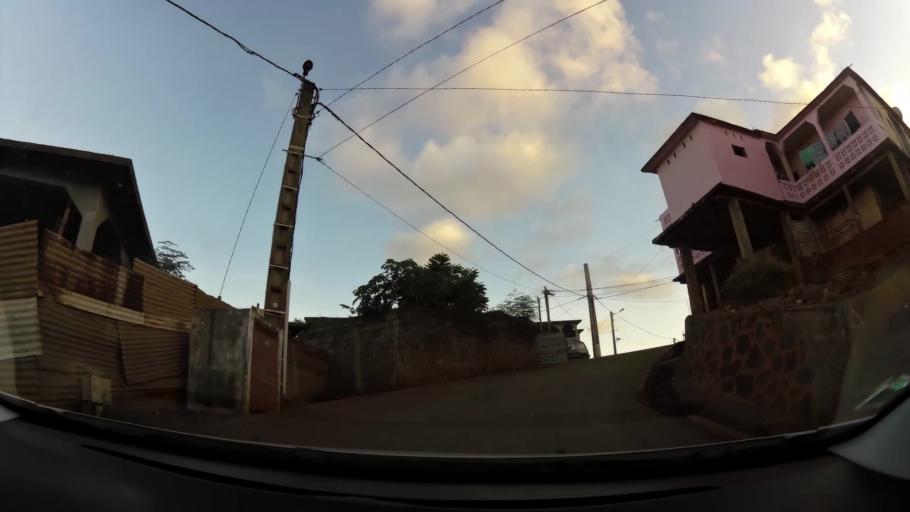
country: YT
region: Dembeni
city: Dembeni
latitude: -12.8676
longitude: 45.1959
